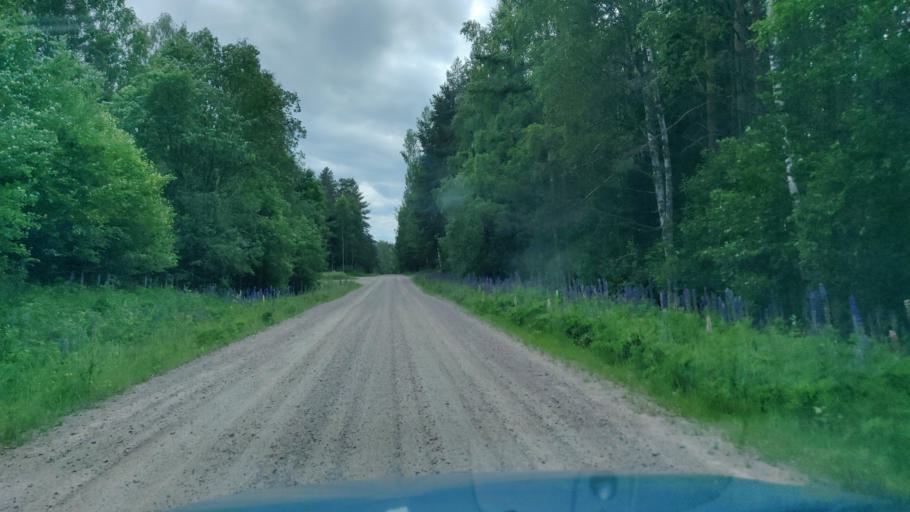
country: SE
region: Vaermland
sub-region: Hagfors Kommun
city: Hagfors
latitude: 60.0338
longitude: 13.7168
